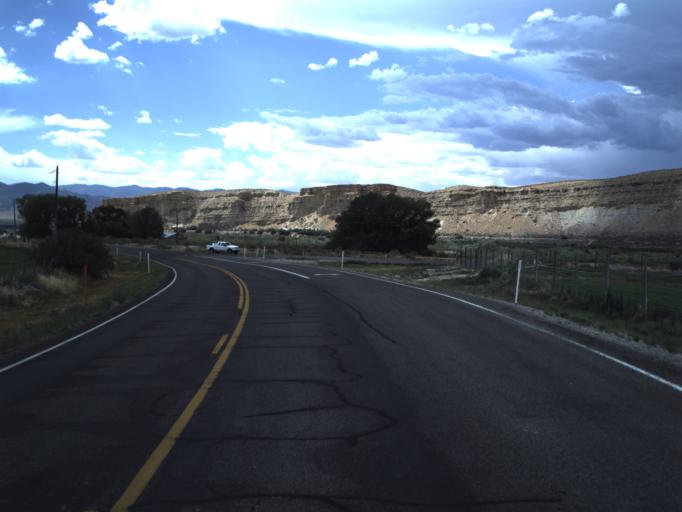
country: US
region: Utah
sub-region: Sanpete County
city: Gunnison
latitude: 39.1445
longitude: -111.7613
